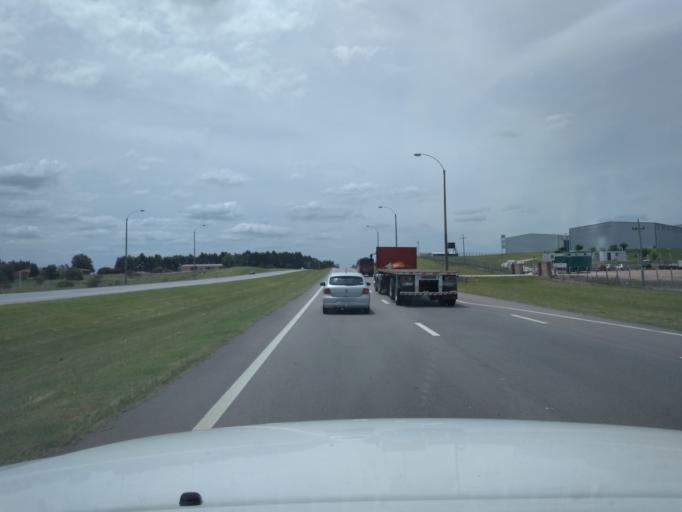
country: UY
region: Canelones
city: Progreso
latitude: -34.6891
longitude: -56.2393
